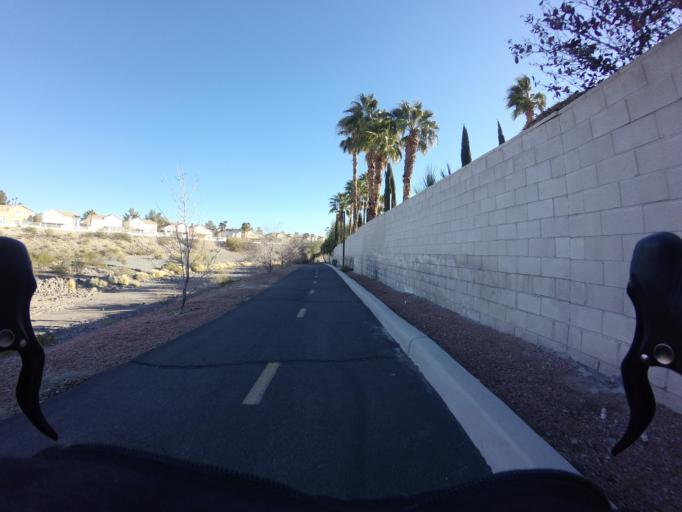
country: US
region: Nevada
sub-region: Clark County
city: Whitney
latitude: 36.0399
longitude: -115.0946
